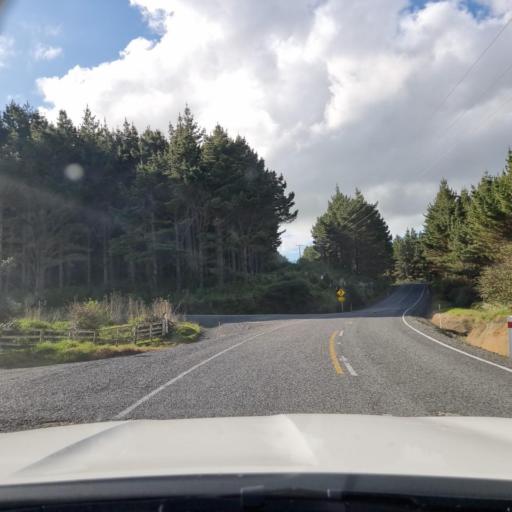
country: NZ
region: Northland
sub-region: Kaipara District
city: Dargaville
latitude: -36.2470
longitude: 174.0432
